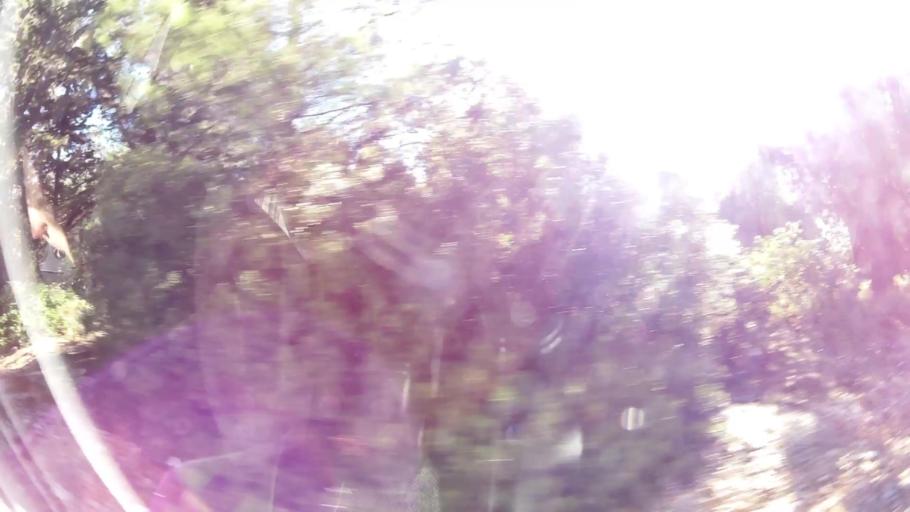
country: GR
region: Attica
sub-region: Nomarchia Anatolikis Attikis
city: Varybobi
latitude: 38.1291
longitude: 23.7953
